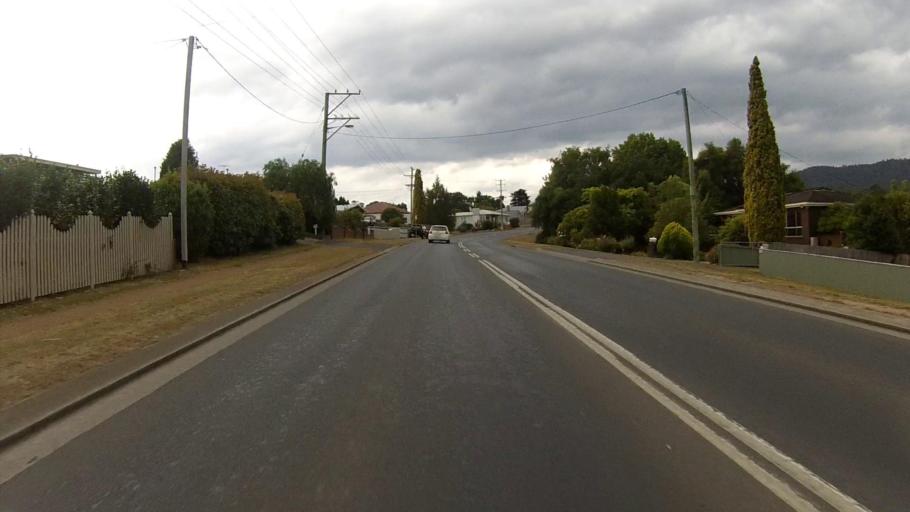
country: AU
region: Tasmania
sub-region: Huon Valley
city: Huonville
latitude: -43.0209
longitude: 147.0538
